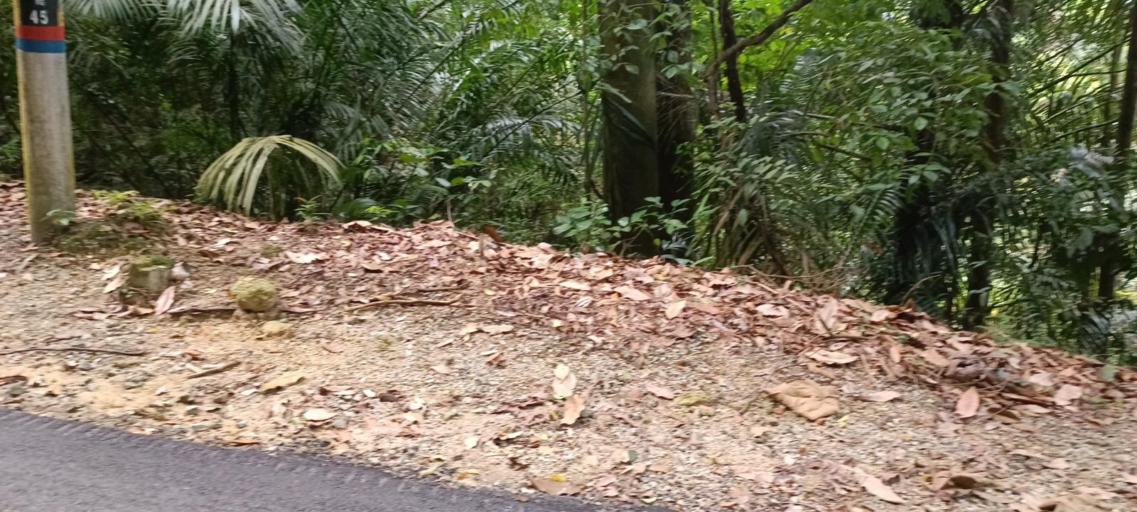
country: MY
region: Perak
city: Taiping
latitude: 4.8605
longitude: 100.7666
